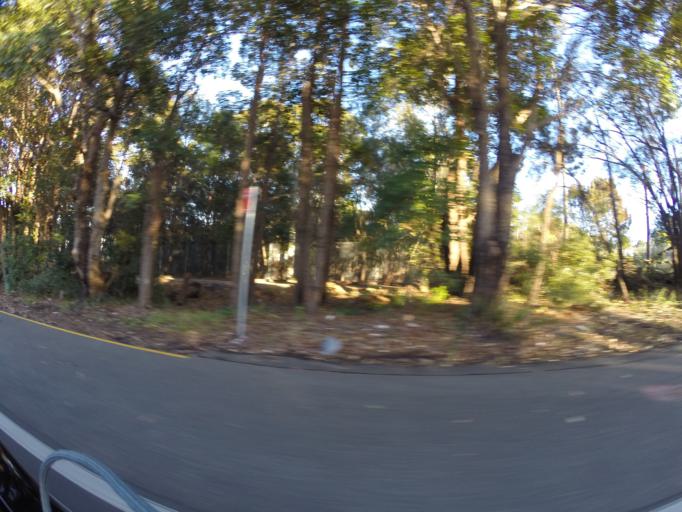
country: AU
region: New South Wales
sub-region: Sutherland Shire
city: Loftus
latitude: -34.0373
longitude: 151.0544
